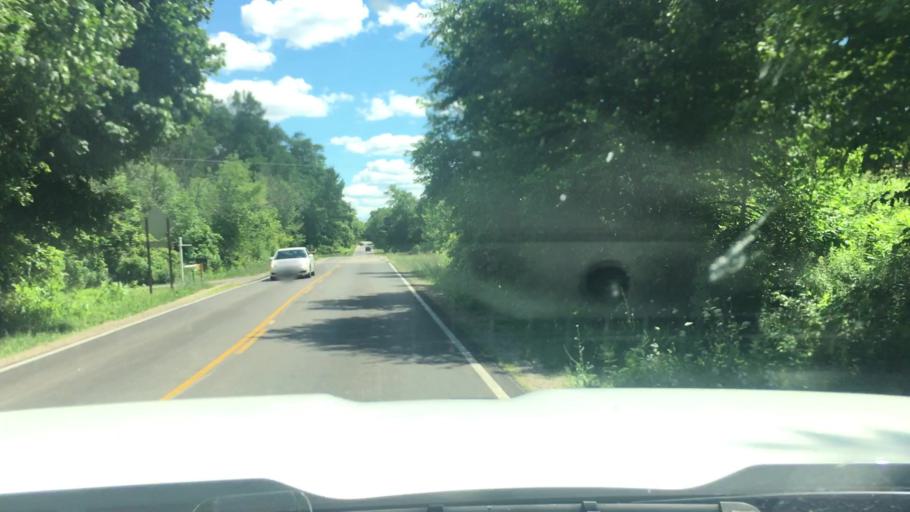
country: US
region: Michigan
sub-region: Kent County
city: Sparta
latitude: 43.1586
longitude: -85.6411
